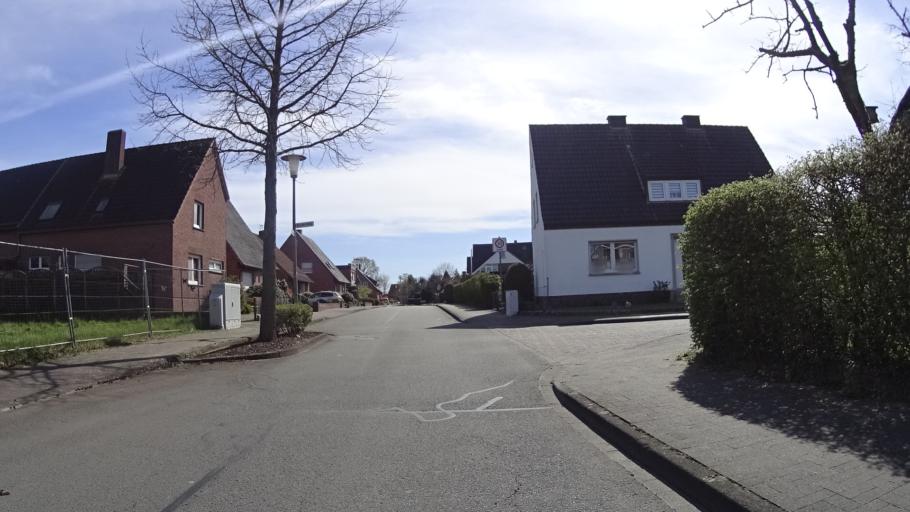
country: DE
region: North Rhine-Westphalia
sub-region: Regierungsbezirk Munster
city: Dreierwalde
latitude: 52.2793
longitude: 7.4778
